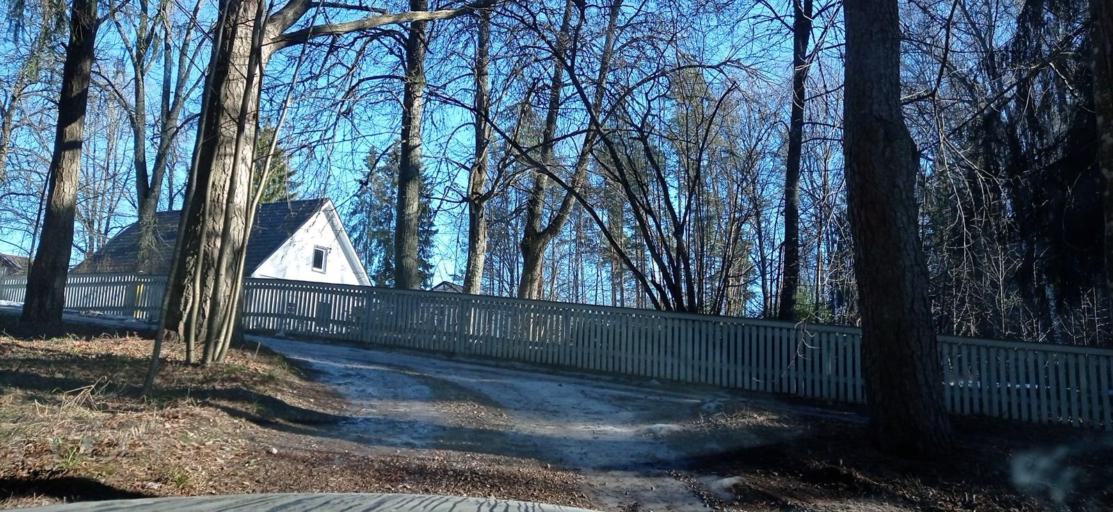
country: EE
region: Tartu
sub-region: Elva linn
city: Elva
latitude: 58.2365
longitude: 26.4403
